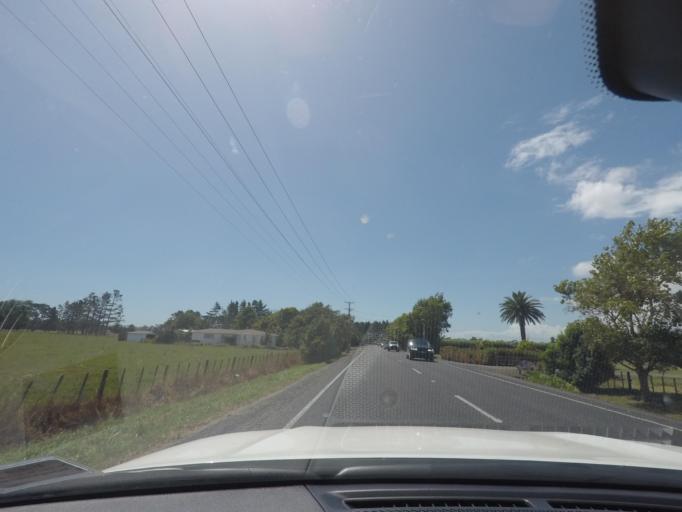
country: NZ
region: Auckland
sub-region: Auckland
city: Parakai
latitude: -36.6683
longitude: 174.4379
